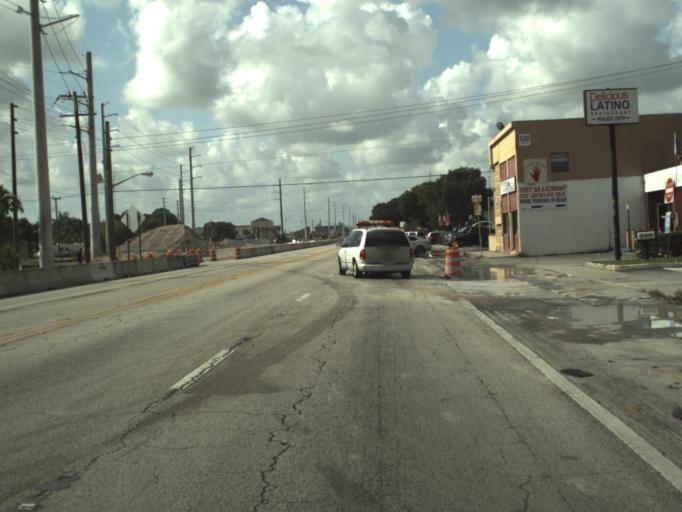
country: US
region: Florida
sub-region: Broward County
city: Pembroke Pines
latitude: 26.0145
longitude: -80.2079
